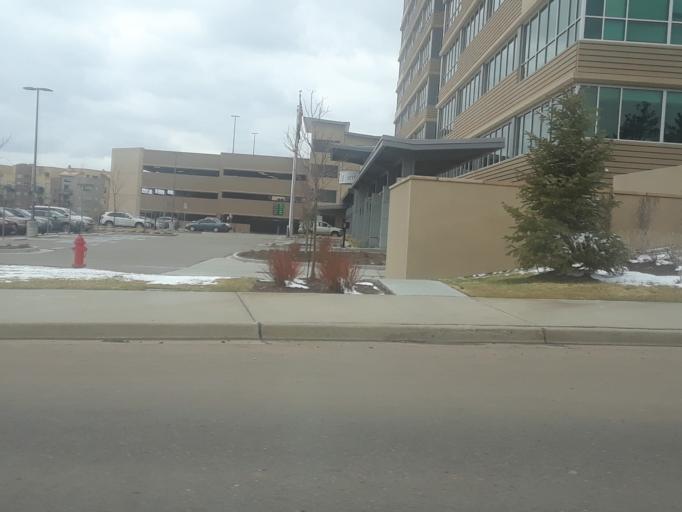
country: US
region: Colorado
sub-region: Arapahoe County
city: Centennial
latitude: 39.5798
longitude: -104.8812
